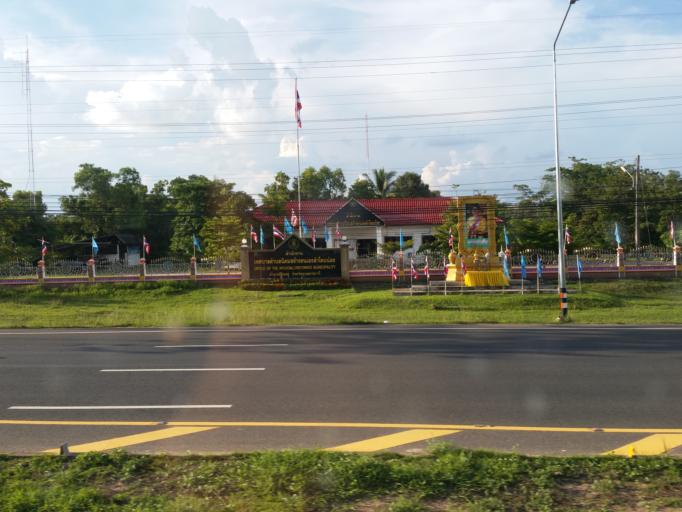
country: TH
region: Changwat Ubon Ratchathani
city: Sirindhorn
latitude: 15.2007
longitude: 105.3884
